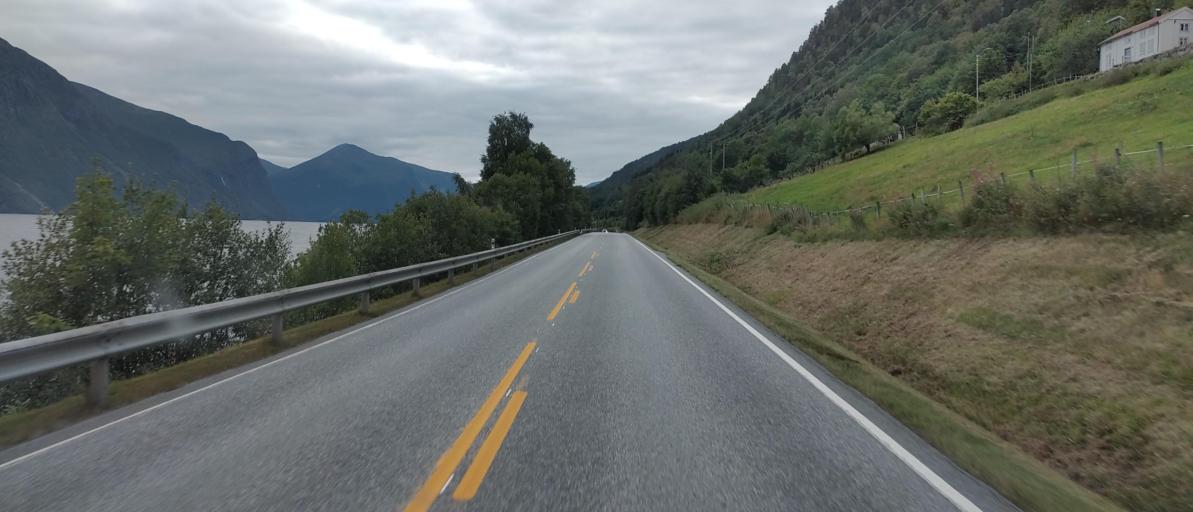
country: NO
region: More og Romsdal
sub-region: Rauma
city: Andalsnes
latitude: 62.5805
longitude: 7.6891
